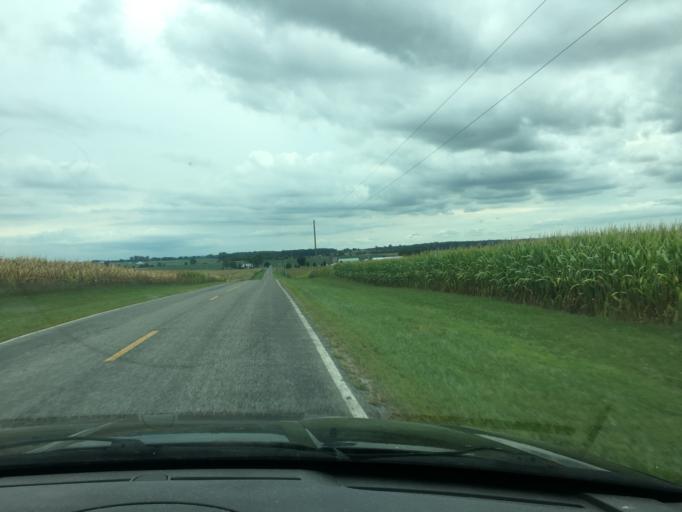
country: US
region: Ohio
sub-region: Logan County
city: West Liberty
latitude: 40.1918
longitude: -83.7506
